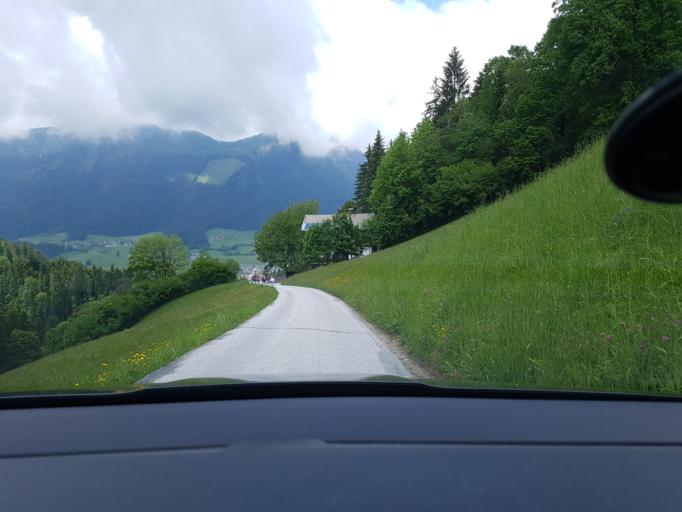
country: AT
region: Tyrol
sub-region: Politischer Bezirk Kufstein
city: Soll
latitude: 47.4920
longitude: 12.2031
